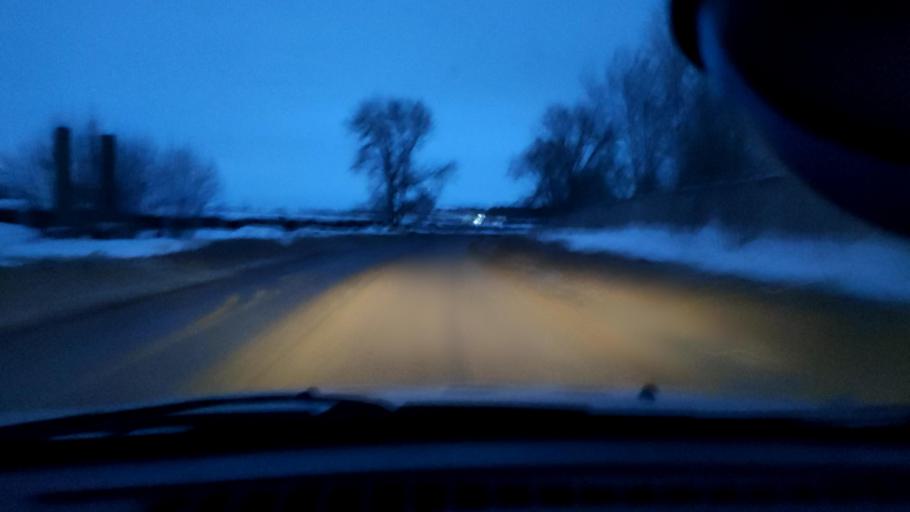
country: RU
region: Perm
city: Overyata
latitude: 58.0004
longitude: 55.9131
